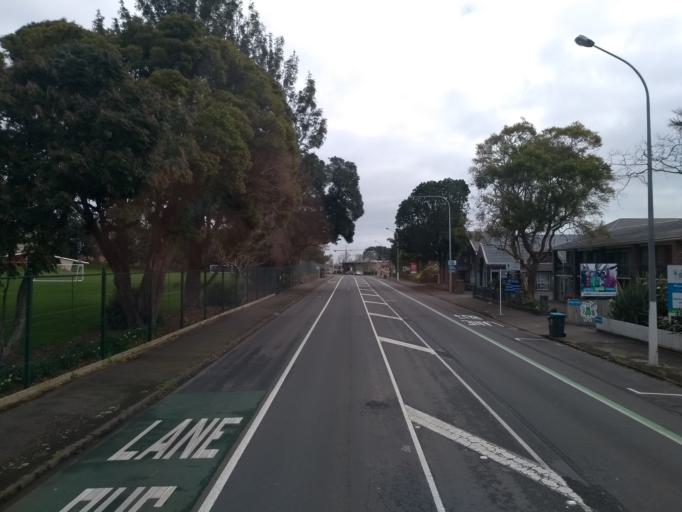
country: NZ
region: Auckland
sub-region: Auckland
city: Auckland
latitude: -36.8809
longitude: 174.7836
